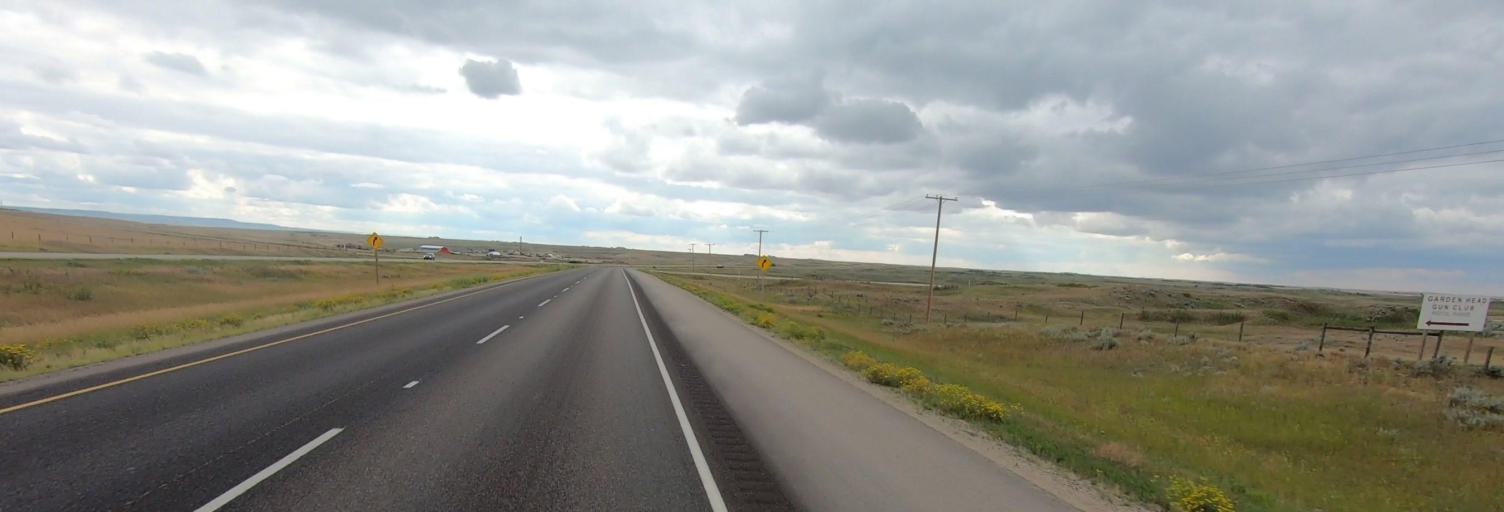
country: CA
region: Saskatchewan
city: Shaunavon
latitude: 50.0734
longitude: -108.5746
